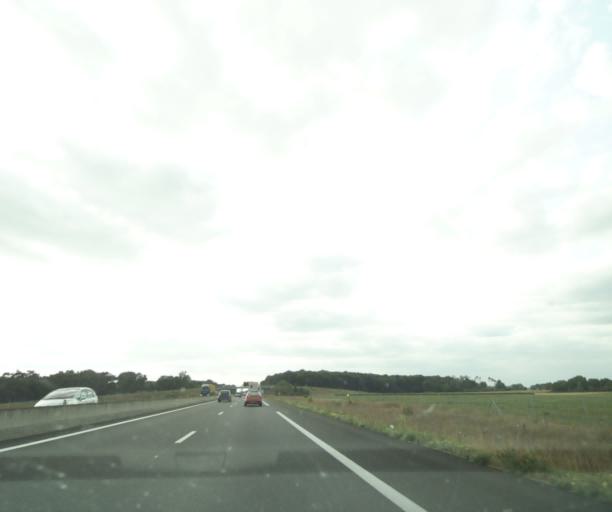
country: FR
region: Centre
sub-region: Departement d'Indre-et-Loire
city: Esvres
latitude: 47.3121
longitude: 0.7758
